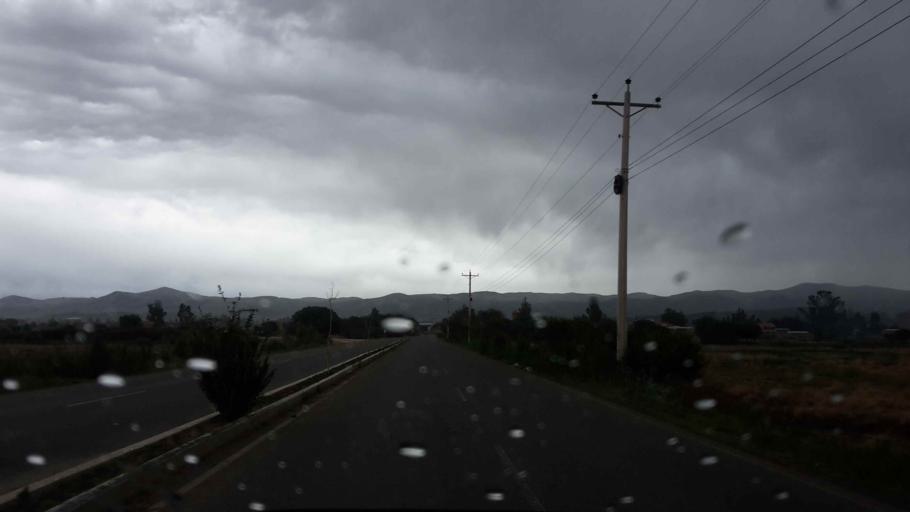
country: BO
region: Cochabamba
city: Tarata
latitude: -17.5578
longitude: -66.0082
